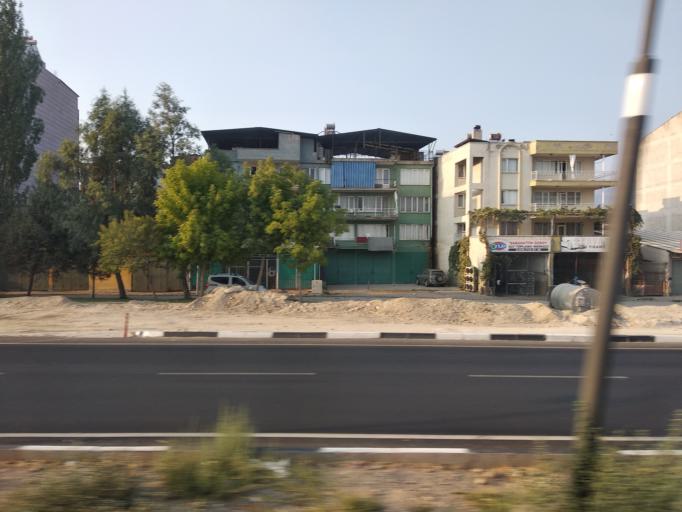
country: TR
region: Manisa
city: Salihli
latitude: 38.4900
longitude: 28.1458
